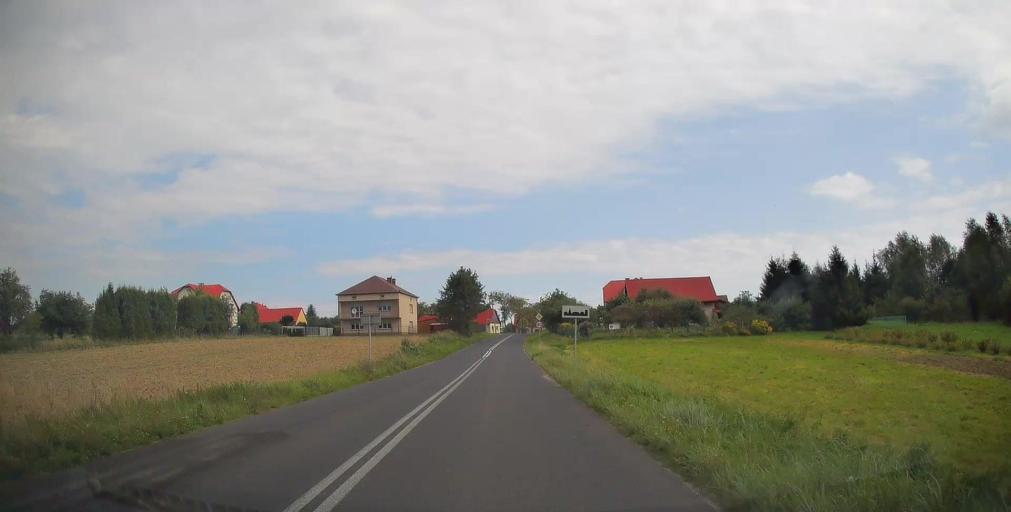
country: PL
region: Lesser Poland Voivodeship
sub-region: Powiat chrzanowski
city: Grojec
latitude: 50.0875
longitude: 19.5545
